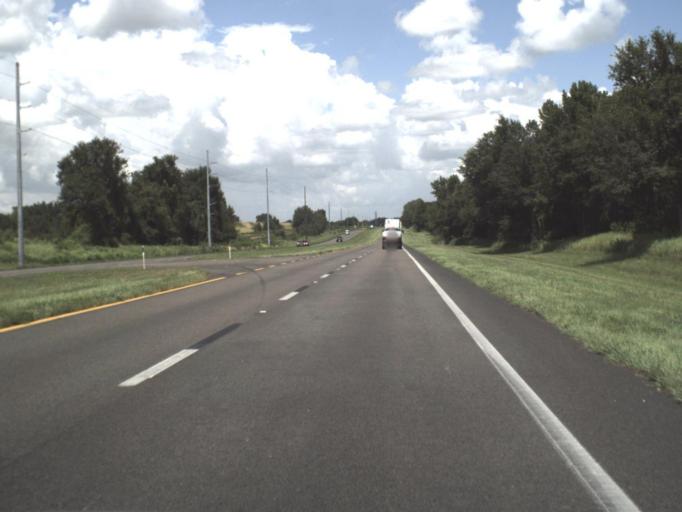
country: US
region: Florida
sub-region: Polk County
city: Fort Meade
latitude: 27.7921
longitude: -81.8147
